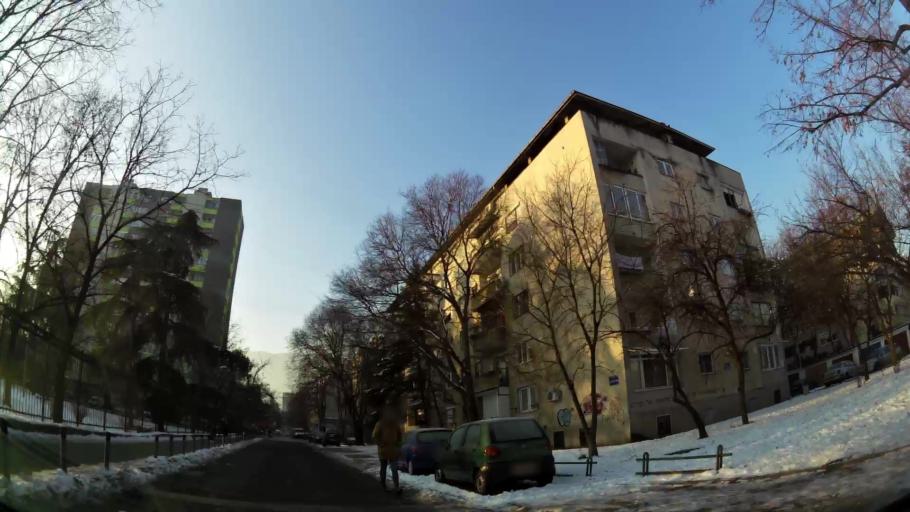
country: MK
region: Karpos
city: Skopje
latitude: 42.0041
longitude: 21.4077
